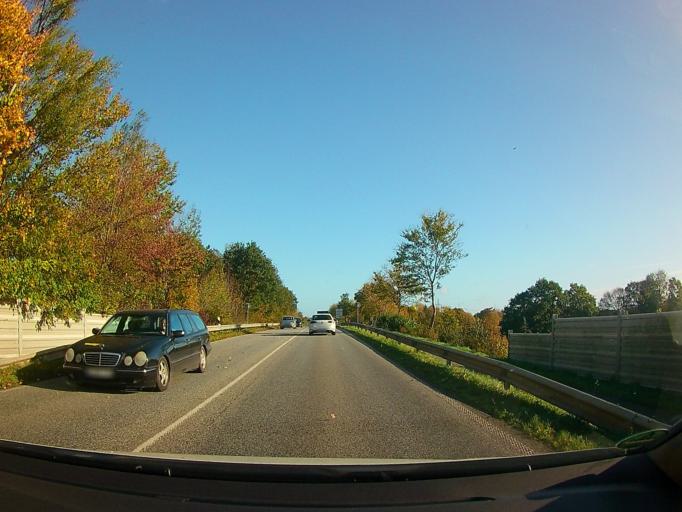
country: DE
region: Schleswig-Holstein
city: Schuby
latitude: 54.5220
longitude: 9.4836
